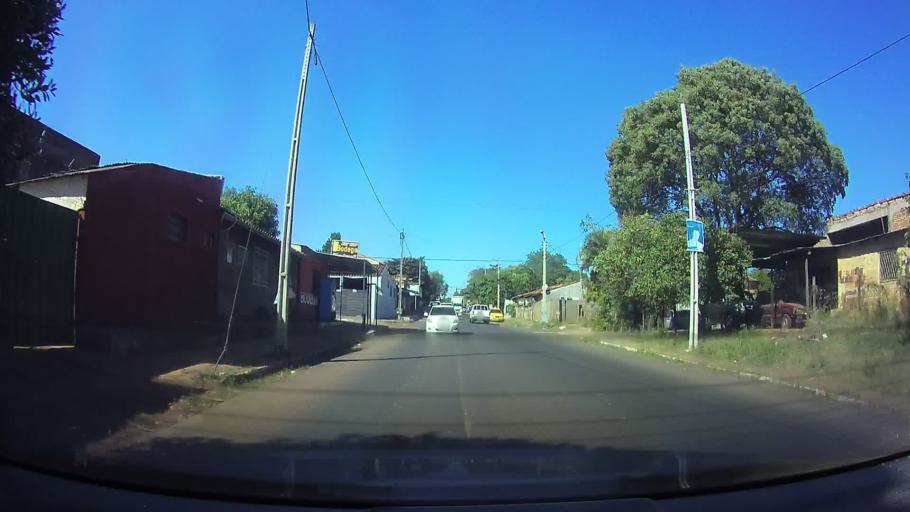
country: PY
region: Central
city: Lambare
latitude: -25.3446
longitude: -57.5854
